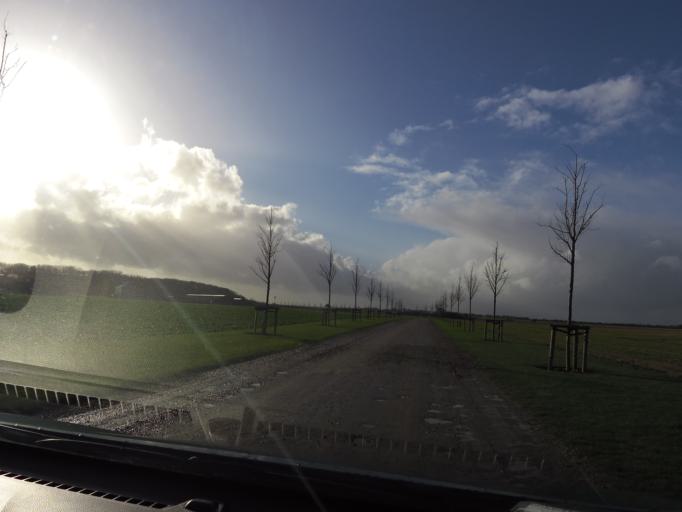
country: DK
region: Central Jutland
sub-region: Odder Kommune
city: Odder
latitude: 55.8662
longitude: 10.1677
